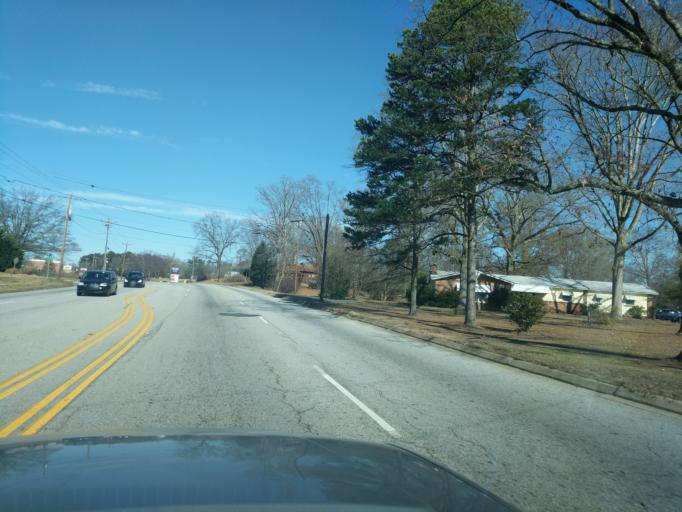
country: US
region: South Carolina
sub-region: Spartanburg County
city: Mayo
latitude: 35.0229
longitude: -81.8954
